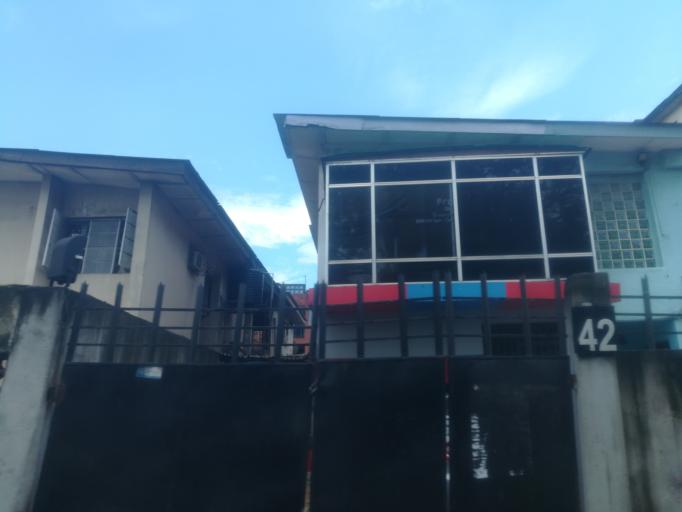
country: NG
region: Lagos
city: Somolu
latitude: 6.5622
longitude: 3.3701
